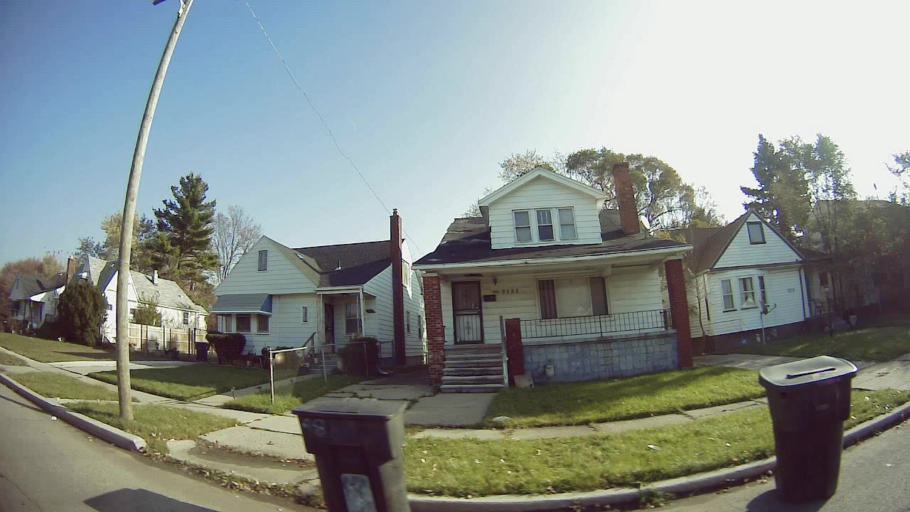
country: US
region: Michigan
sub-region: Wayne County
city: Dearborn
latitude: 42.3674
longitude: -83.1679
